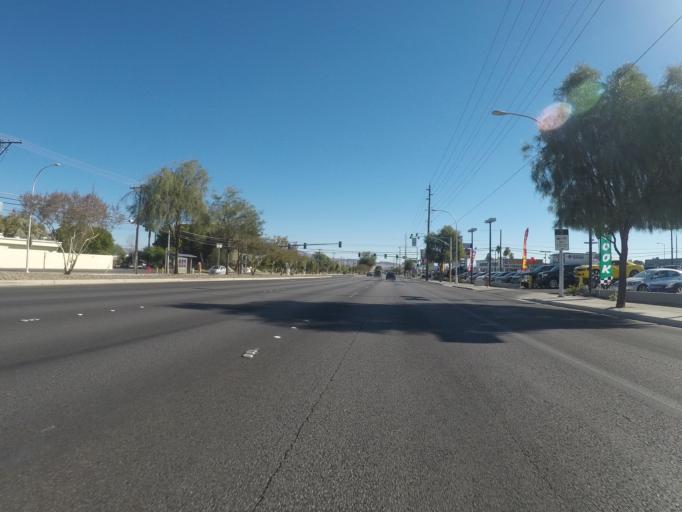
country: US
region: Nevada
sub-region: Clark County
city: Winchester
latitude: 36.1443
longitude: -115.1155
